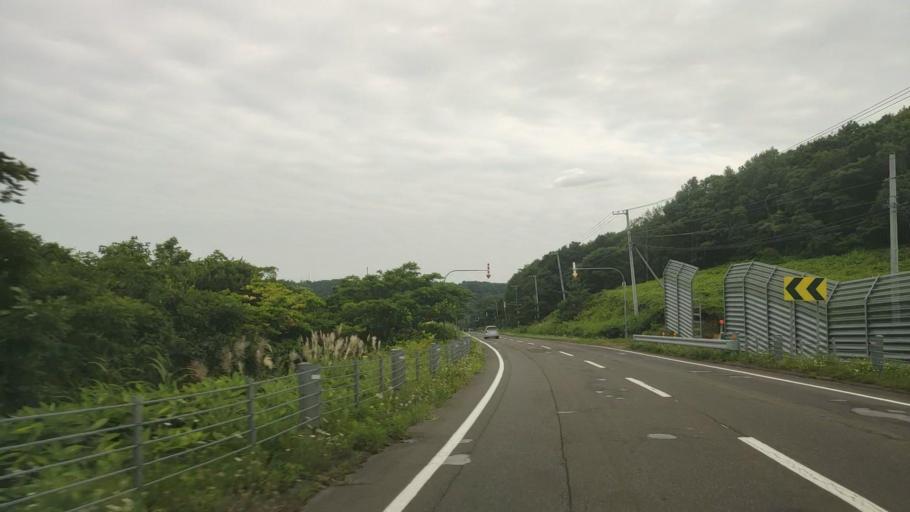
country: JP
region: Hokkaido
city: Ishikari
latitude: 43.3304
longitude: 141.4416
